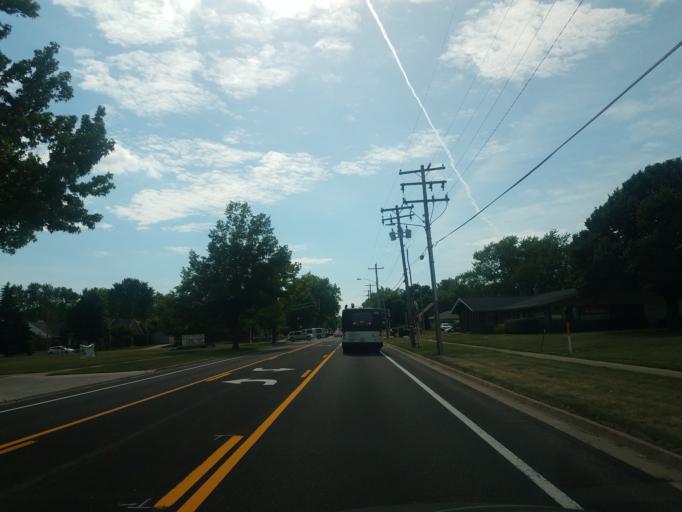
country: US
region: Illinois
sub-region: McLean County
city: Bloomington
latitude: 40.4801
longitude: -88.9582
